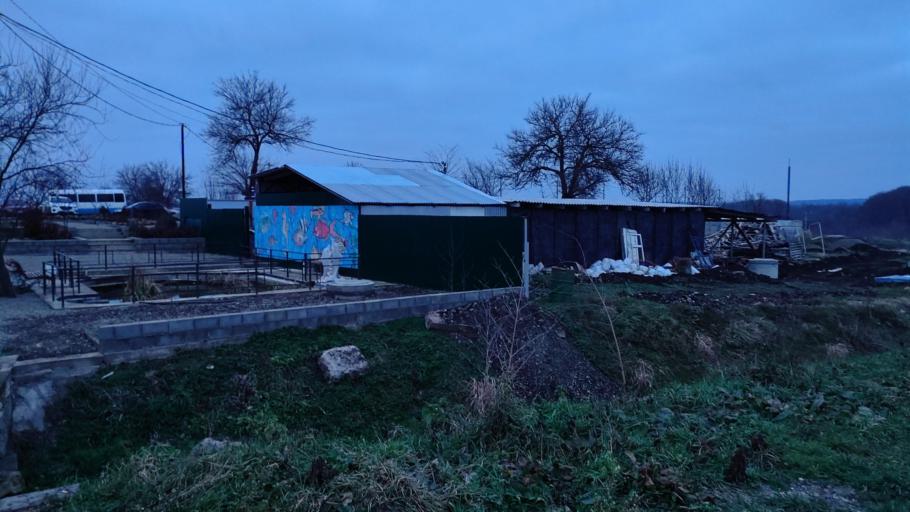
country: RU
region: Krasnodarskiy
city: Yaroslavskaya
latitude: 44.6048
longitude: 40.4443
